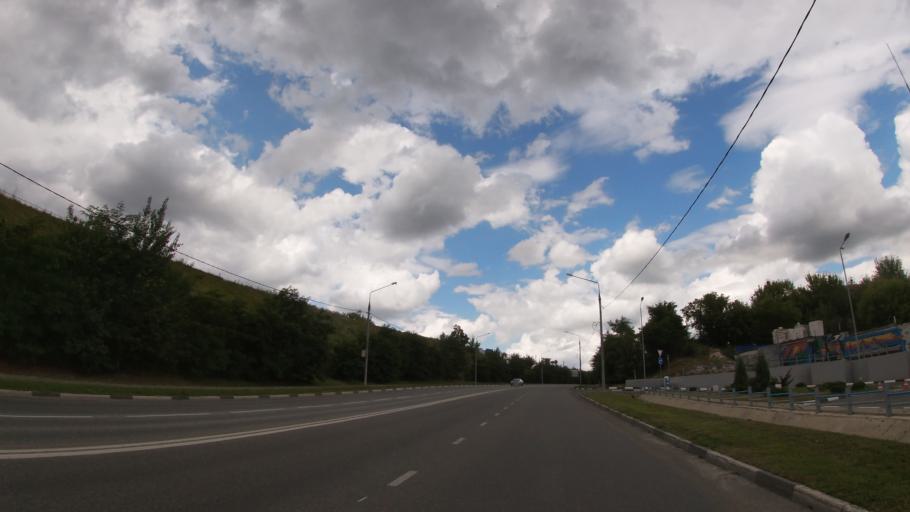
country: RU
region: Belgorod
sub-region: Belgorodskiy Rayon
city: Belgorod
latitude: 50.6100
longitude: 36.6130
